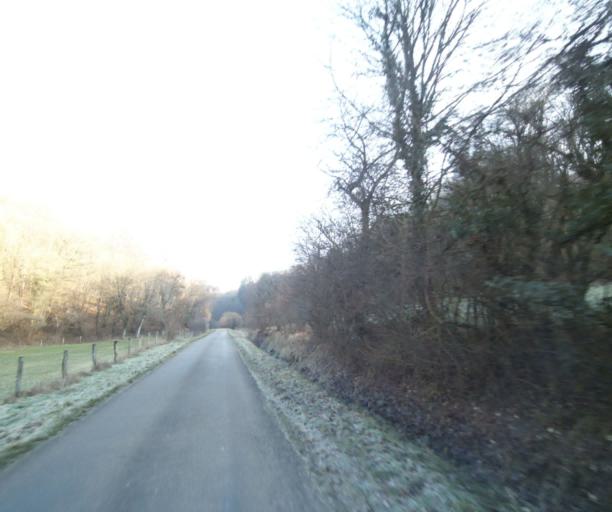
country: FR
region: Champagne-Ardenne
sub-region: Departement de la Haute-Marne
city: Joinville
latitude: 48.4903
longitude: 5.2254
